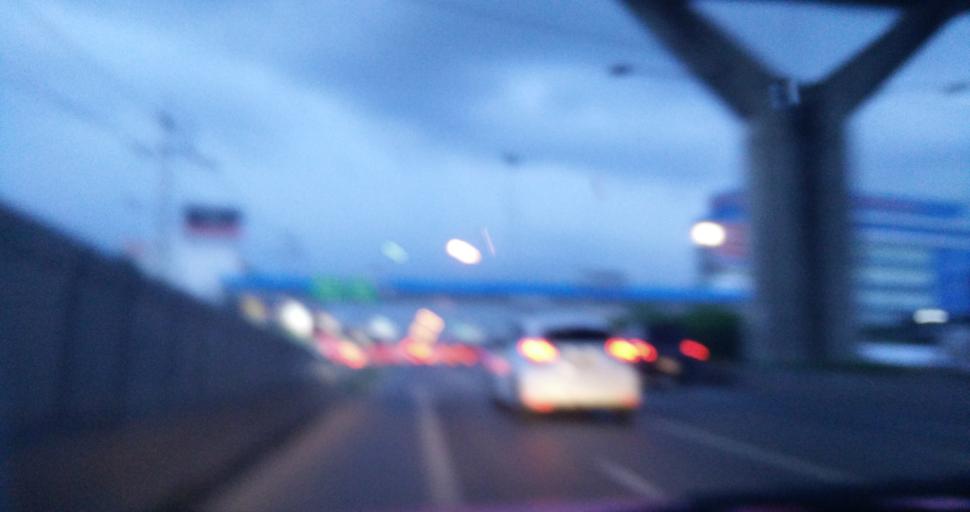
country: TH
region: Phra Nakhon Si Ayutthaya
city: Ban Bang Kadi Pathum Thani
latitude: 14.0056
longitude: 100.6150
